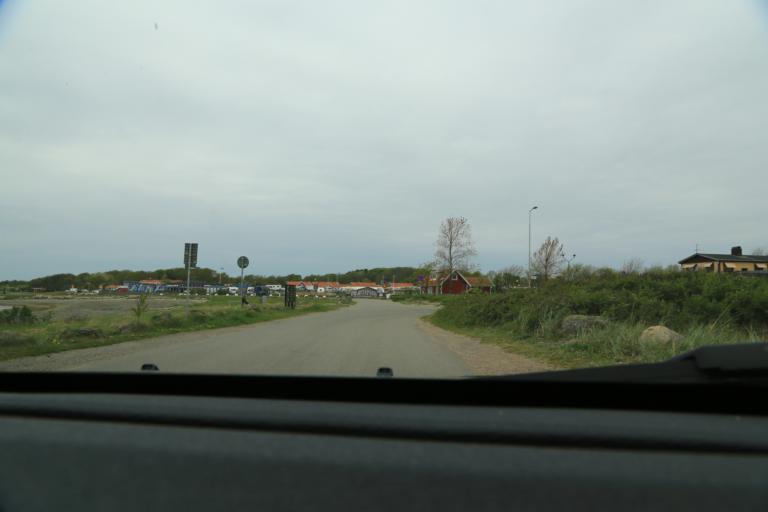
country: SE
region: Halland
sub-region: Varbergs Kommun
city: Varberg
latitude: 57.0851
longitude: 12.2538
